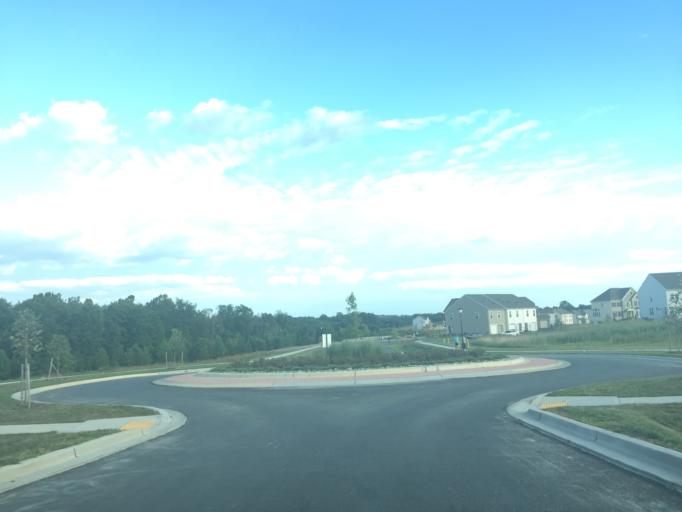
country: US
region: Maryland
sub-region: Montgomery County
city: Redland
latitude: 39.1327
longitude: -77.1147
